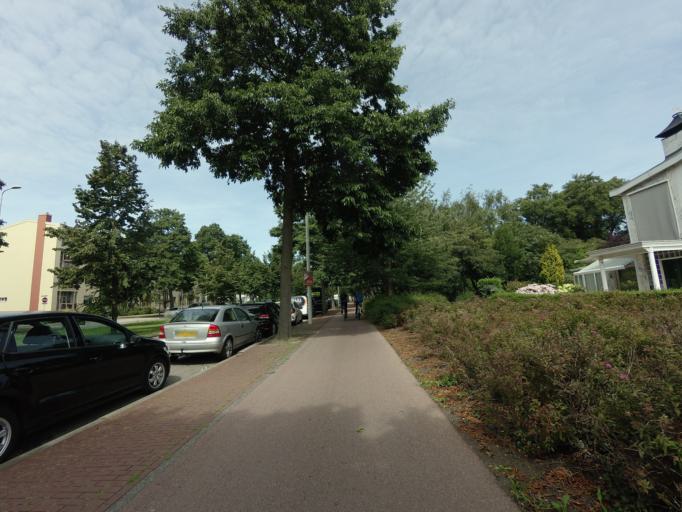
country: NL
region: South Holland
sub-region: Gemeente Den Haag
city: The Hague
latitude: 52.0539
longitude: 4.2779
